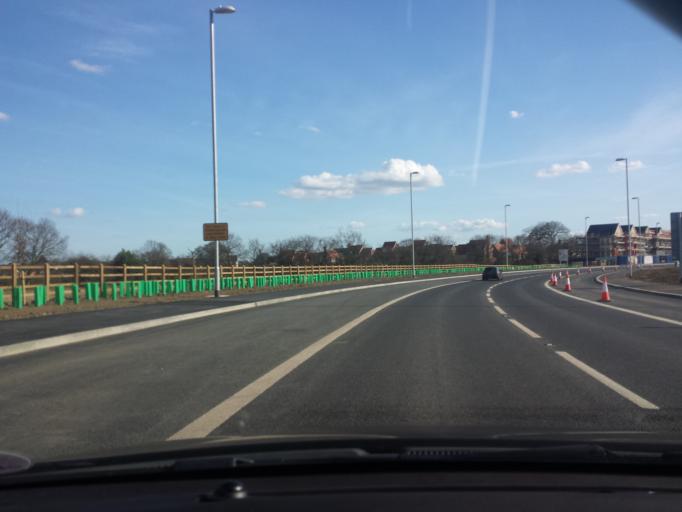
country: GB
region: England
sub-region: Essex
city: Colchester
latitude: 51.9219
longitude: 0.9039
